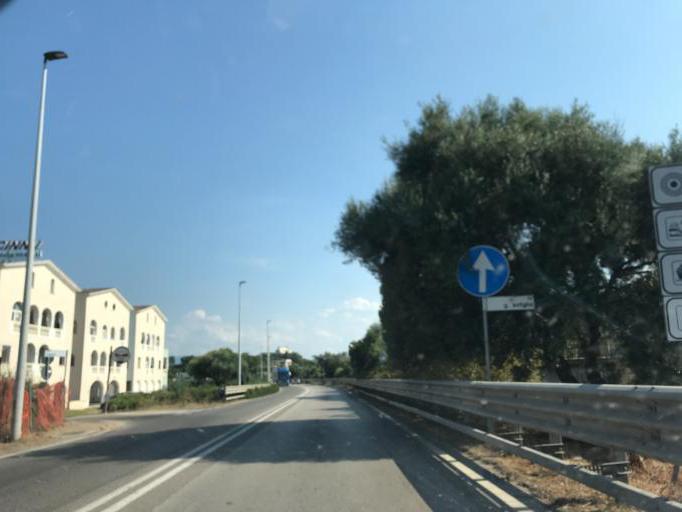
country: IT
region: Sardinia
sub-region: Provincia di Olbia-Tempio
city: Olbia
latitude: 40.9151
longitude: 9.5016
